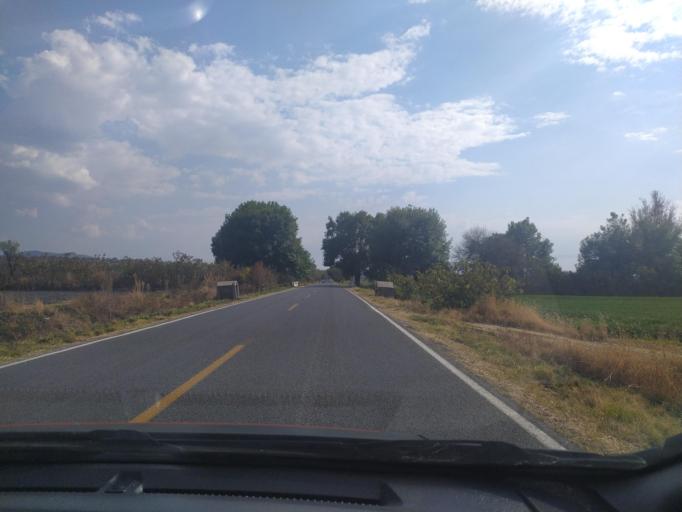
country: MX
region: Guanajuato
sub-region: San Francisco del Rincon
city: San Ignacio de Hidalgo
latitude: 20.8911
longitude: -101.8579
